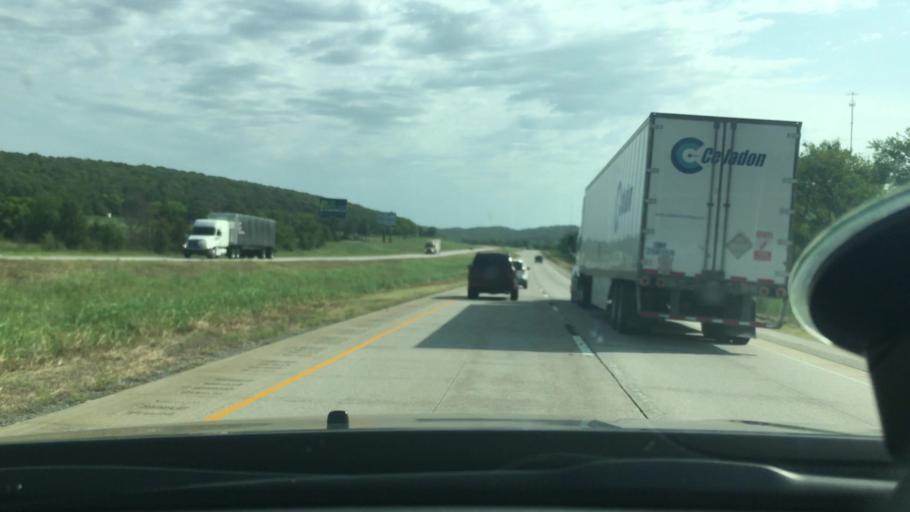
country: US
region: Oklahoma
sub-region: Atoka County
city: Atoka
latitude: 34.4299
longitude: -96.0841
